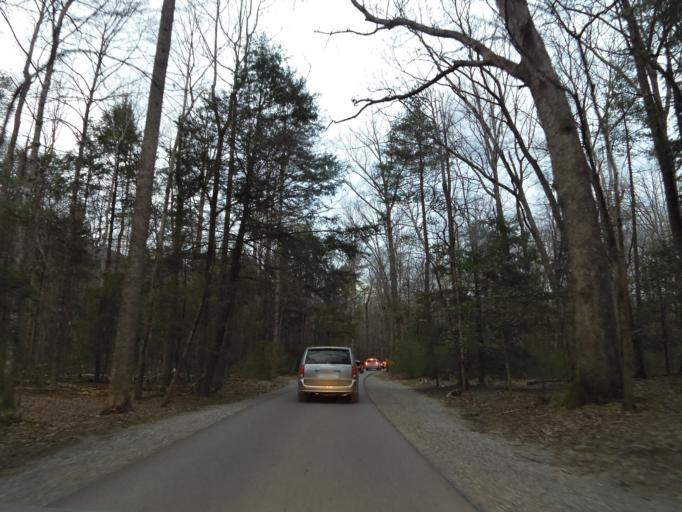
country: US
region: Tennessee
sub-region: Blount County
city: Wildwood
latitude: 35.6038
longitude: -83.7788
